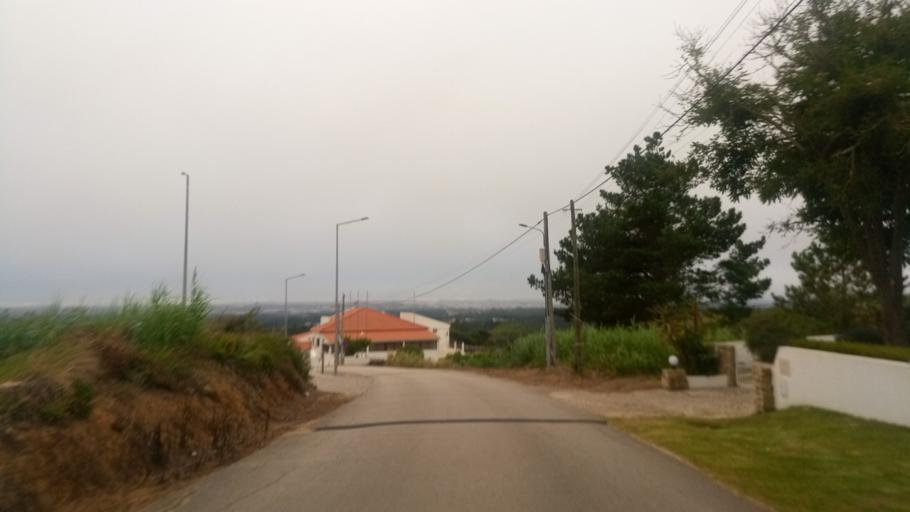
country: PT
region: Leiria
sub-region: Caldas da Rainha
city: Caldas da Rainha
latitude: 39.4602
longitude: -9.1906
